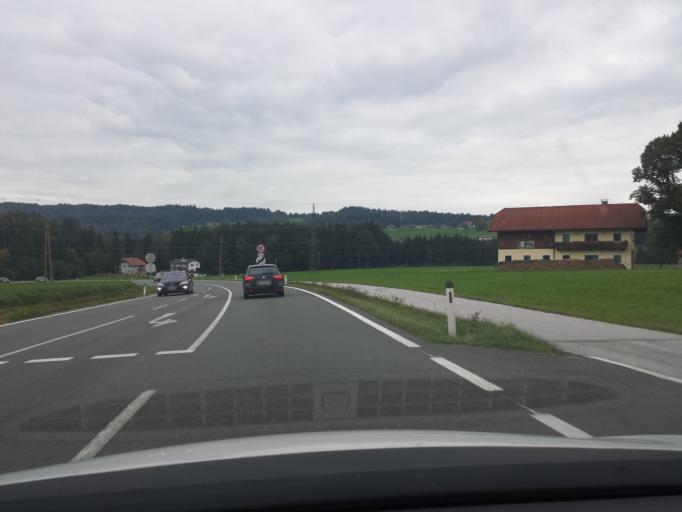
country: AT
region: Salzburg
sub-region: Politischer Bezirk Salzburg-Umgebung
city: Koppl
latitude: 47.8238
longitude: 13.1490
